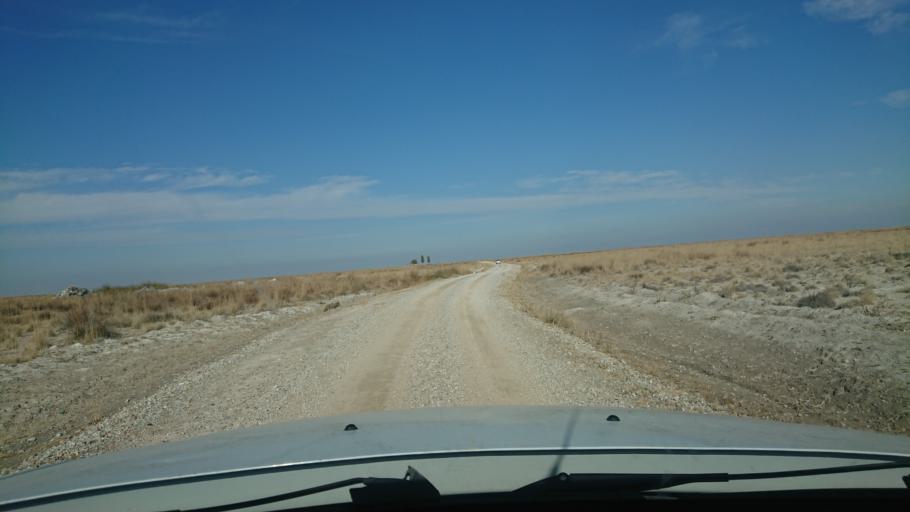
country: TR
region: Aksaray
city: Eskil
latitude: 38.4671
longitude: 33.4549
